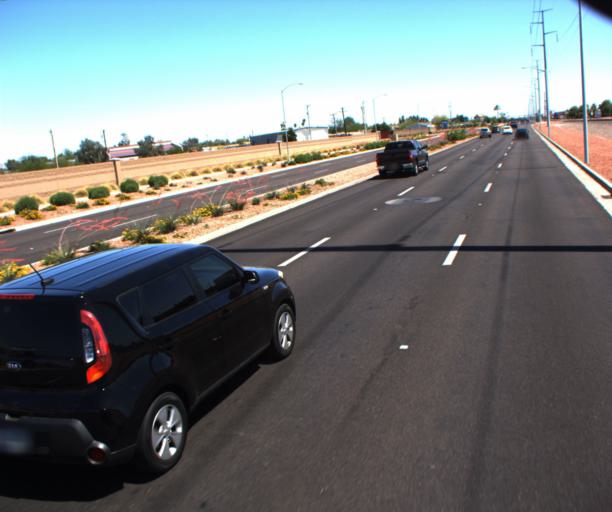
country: US
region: Arizona
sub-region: Maricopa County
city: Glendale
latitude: 33.5475
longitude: -112.1967
